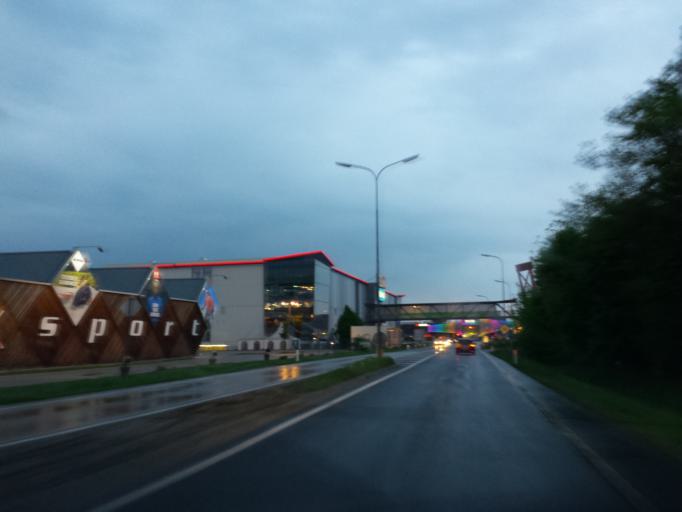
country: AT
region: Lower Austria
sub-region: Politischer Bezirk Modling
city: Wiener Neudorf
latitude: 48.1046
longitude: 16.3114
